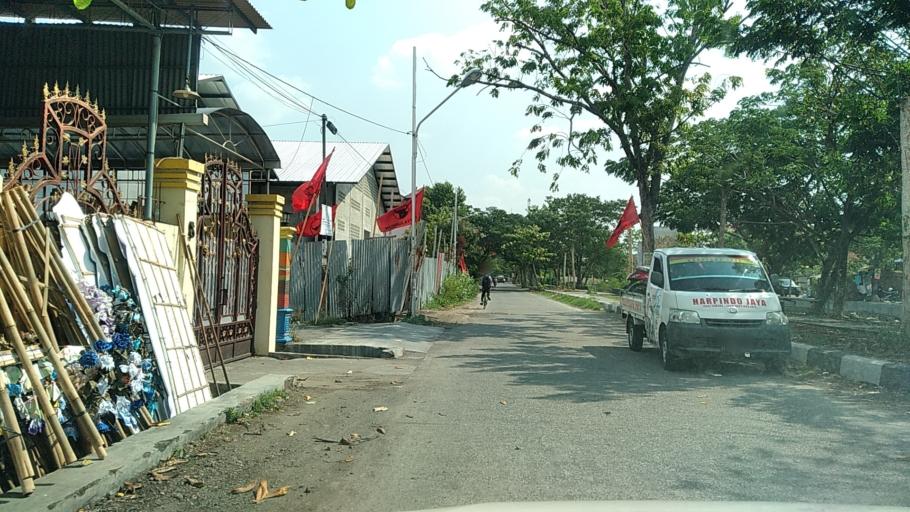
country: ID
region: Central Java
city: Semarang
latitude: -6.9722
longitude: 110.4384
